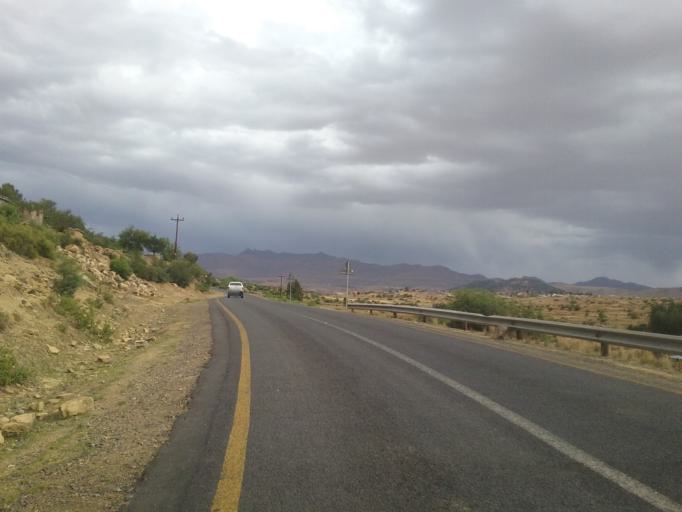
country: LS
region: Quthing
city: Quthing
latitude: -30.3735
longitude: 27.7035
